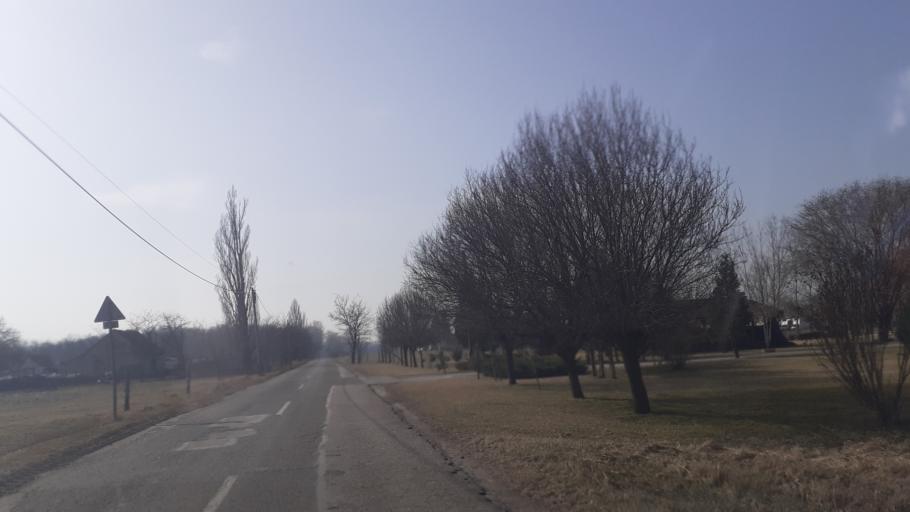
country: HU
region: Pest
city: Orkeny
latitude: 47.0671
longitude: 19.3513
